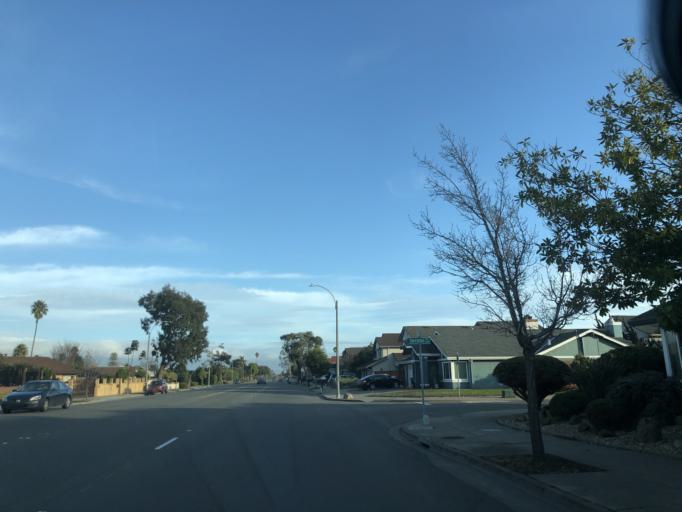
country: US
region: California
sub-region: Alameda County
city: Alameda
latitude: 37.7659
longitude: -122.2700
